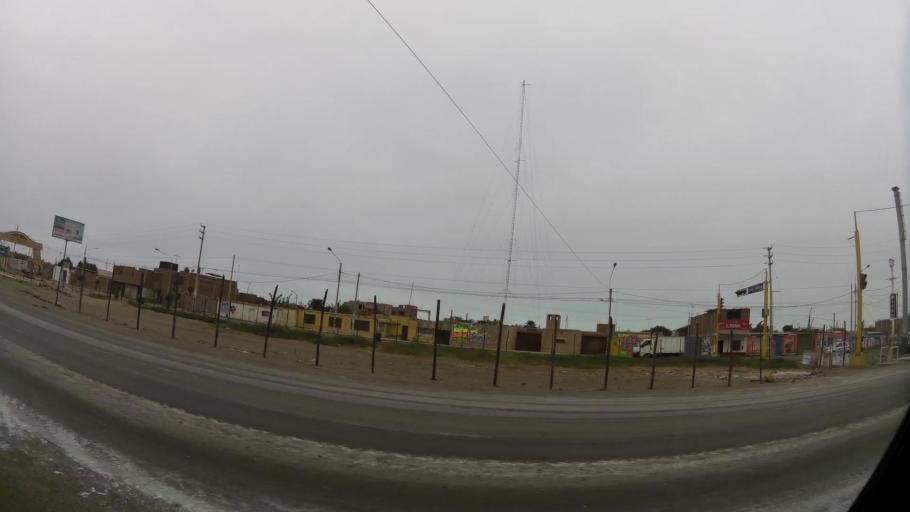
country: PE
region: La Libertad
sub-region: Provincia de Trujillo
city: Moche
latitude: -8.1636
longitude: -79.0101
